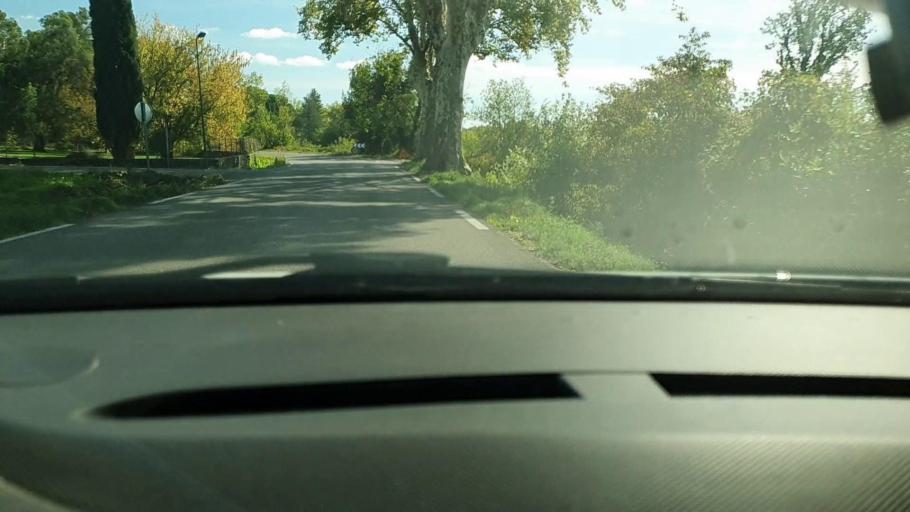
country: FR
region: Languedoc-Roussillon
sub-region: Departement du Gard
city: Saint-Ambroix
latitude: 44.2415
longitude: 4.2211
